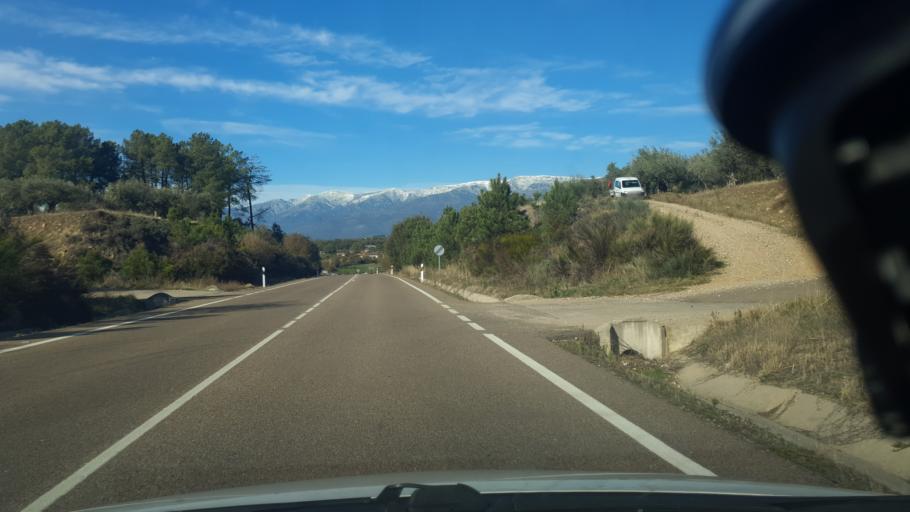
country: ES
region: Castille and Leon
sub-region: Provincia de Avila
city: Candeleda
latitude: 40.1360
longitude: -5.2357
